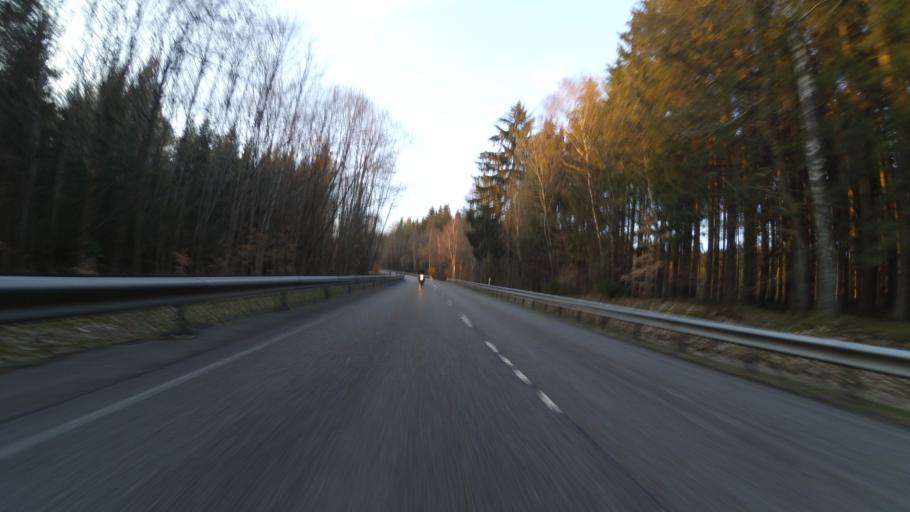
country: DE
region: Rheinland-Pfalz
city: Hattgenstein
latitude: 49.7025
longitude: 7.1450
